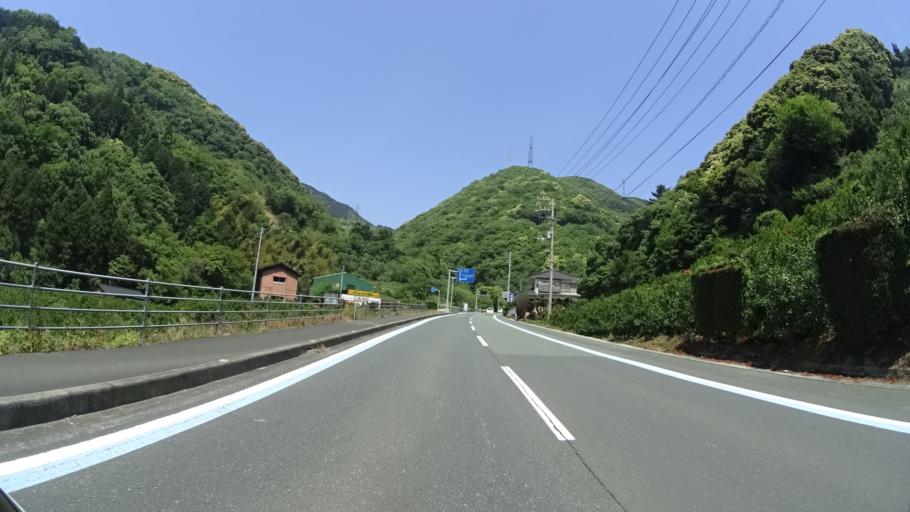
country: JP
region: Ehime
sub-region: Nishiuwa-gun
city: Ikata-cho
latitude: 33.5065
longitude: 132.3977
